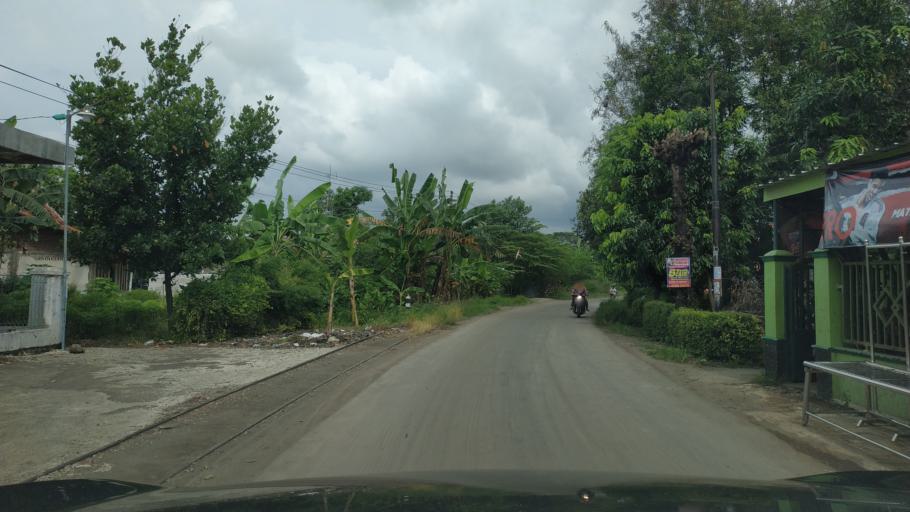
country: ID
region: Central Java
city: Pemalang
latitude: -6.9174
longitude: 109.3287
